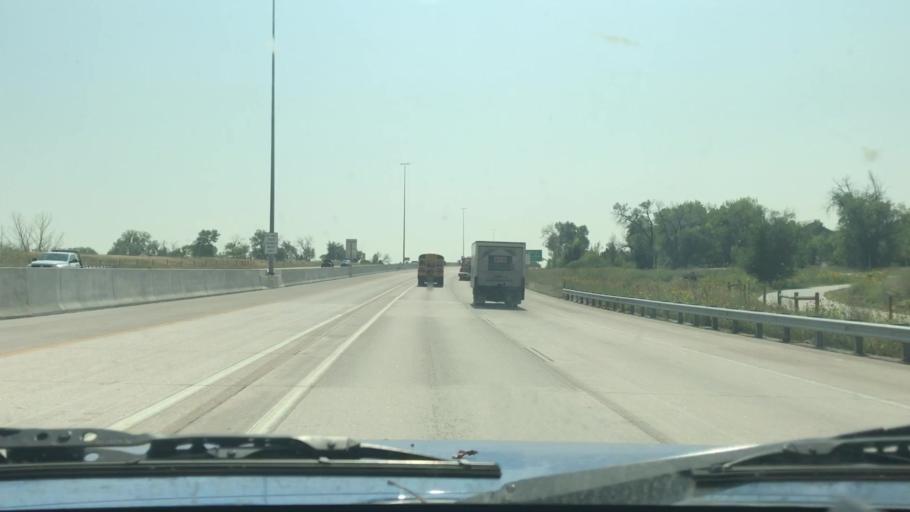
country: US
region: Colorado
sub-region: Adams County
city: Westminster
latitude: 39.8723
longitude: -105.0613
